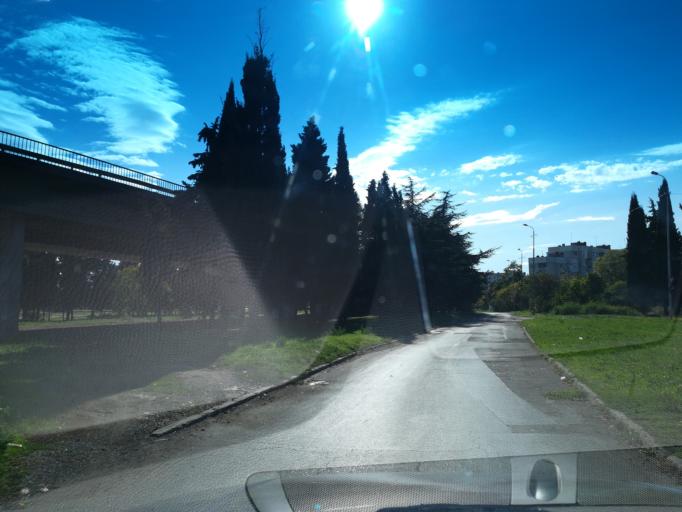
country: BG
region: Stara Zagora
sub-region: Obshtina Stara Zagora
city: Stara Zagora
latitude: 42.4270
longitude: 25.6478
